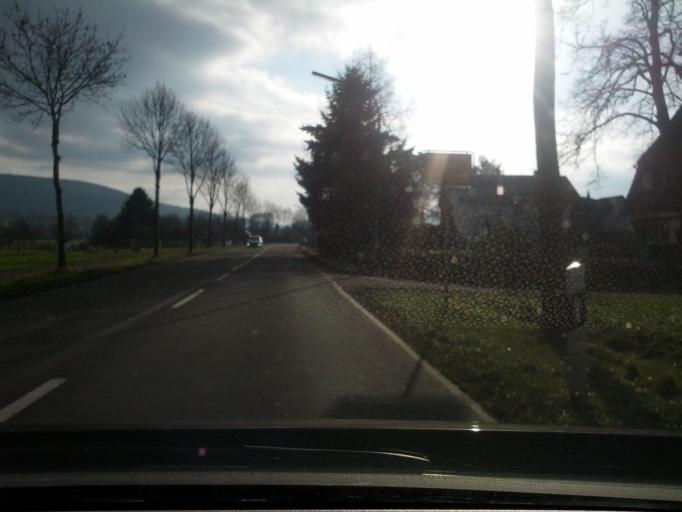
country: DE
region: Lower Saxony
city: Buhren
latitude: 51.5027
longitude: 9.5990
